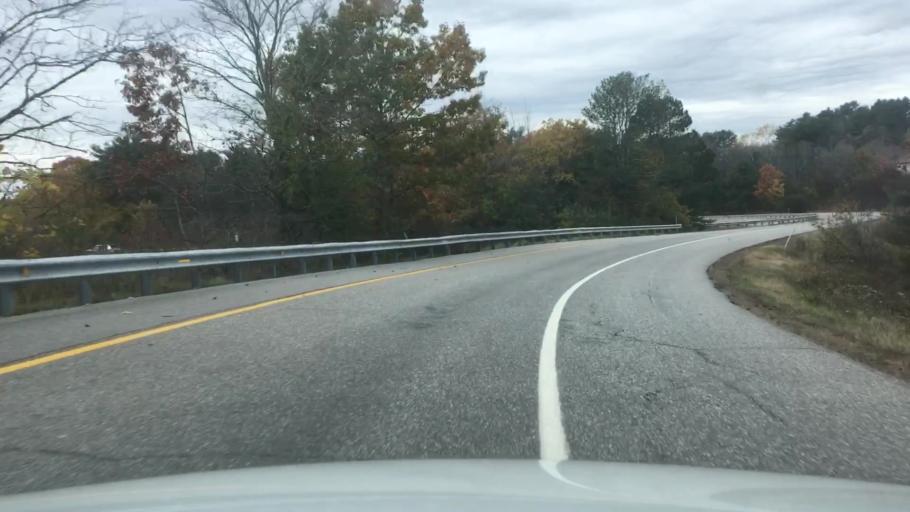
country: US
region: Maine
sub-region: Cumberland County
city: Falmouth
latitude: 43.7296
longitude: -70.2345
